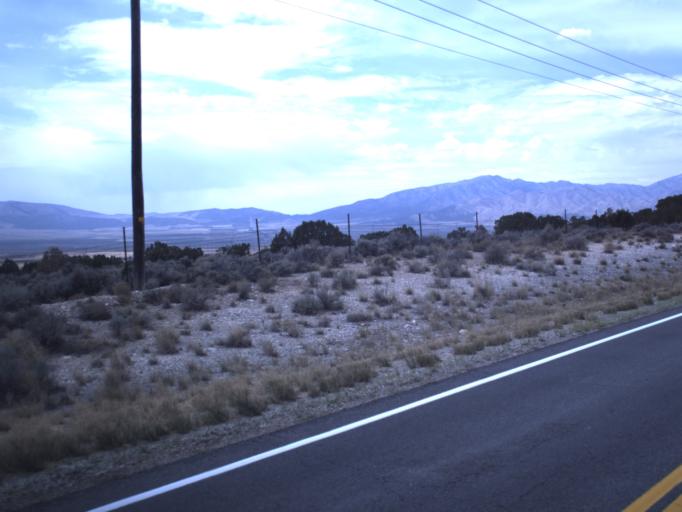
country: US
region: Utah
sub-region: Tooele County
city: Tooele
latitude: 40.3305
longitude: -112.2938
